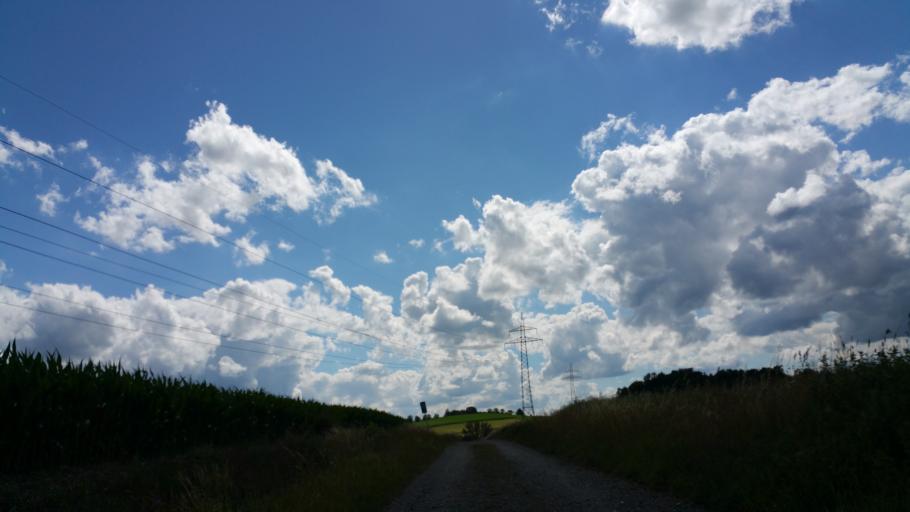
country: DE
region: Bavaria
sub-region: Upper Franconia
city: Schwarzenbach an der Saale
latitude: 50.2349
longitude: 11.9337
